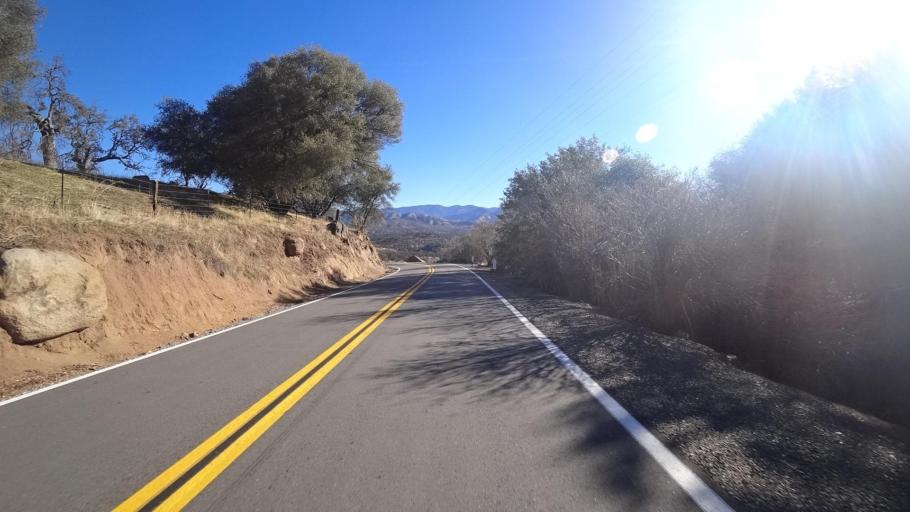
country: US
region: California
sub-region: Kern County
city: Alta Sierra
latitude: 35.7052
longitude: -118.7482
